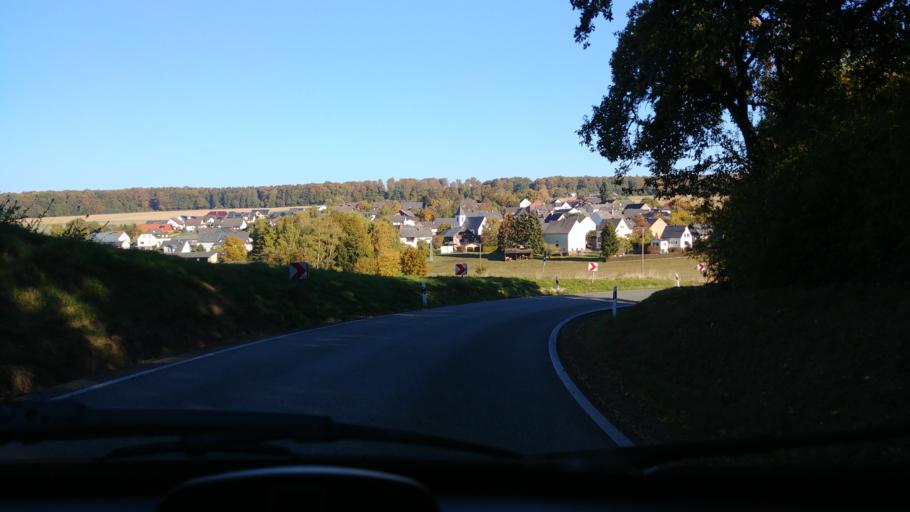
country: DE
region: Rheinland-Pfalz
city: Hunzel
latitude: 50.2441
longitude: 7.8381
